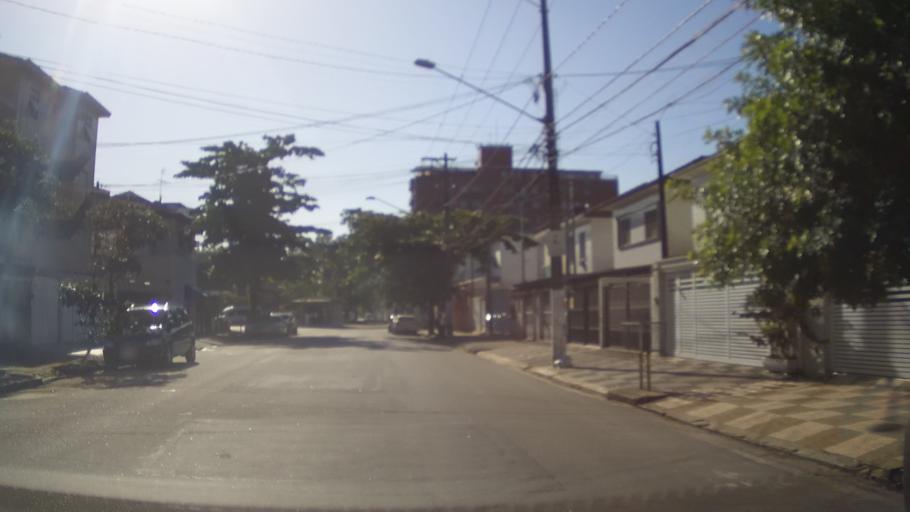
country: BR
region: Sao Paulo
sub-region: Santos
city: Santos
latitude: -23.9517
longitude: -46.3449
